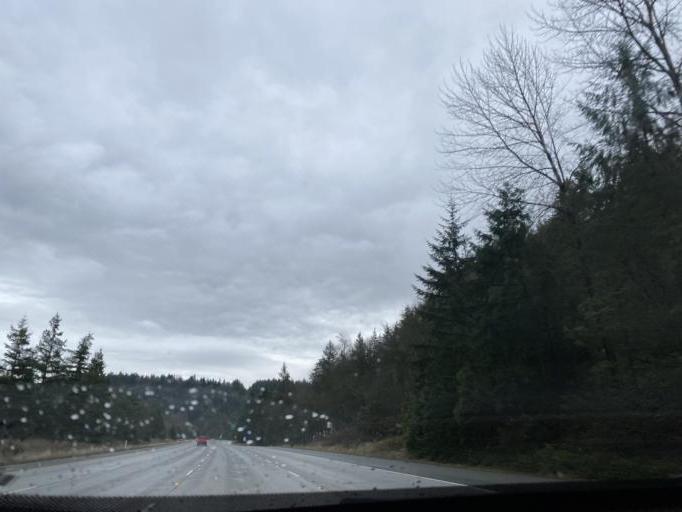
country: US
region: Washington
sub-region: King County
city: Issaquah
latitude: 47.5308
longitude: -121.9899
